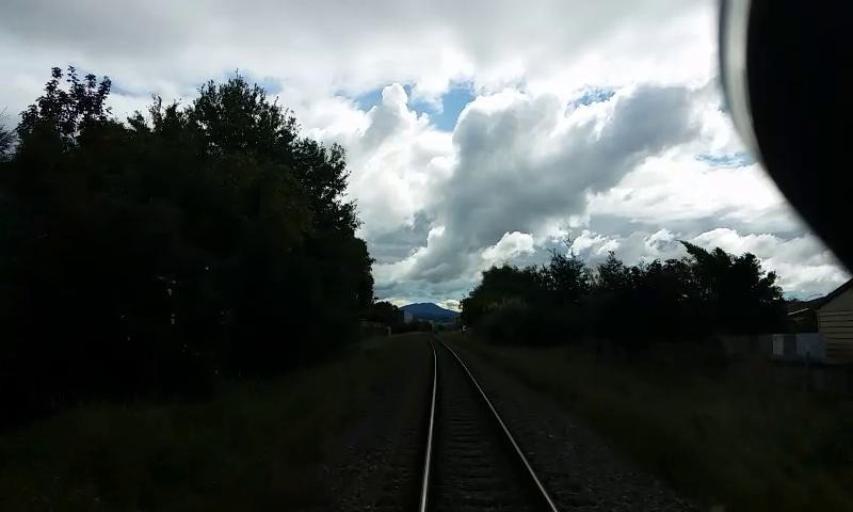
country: NZ
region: Canterbury
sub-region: Waimakariri District
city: Woodend
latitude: -43.3064
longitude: 172.5991
